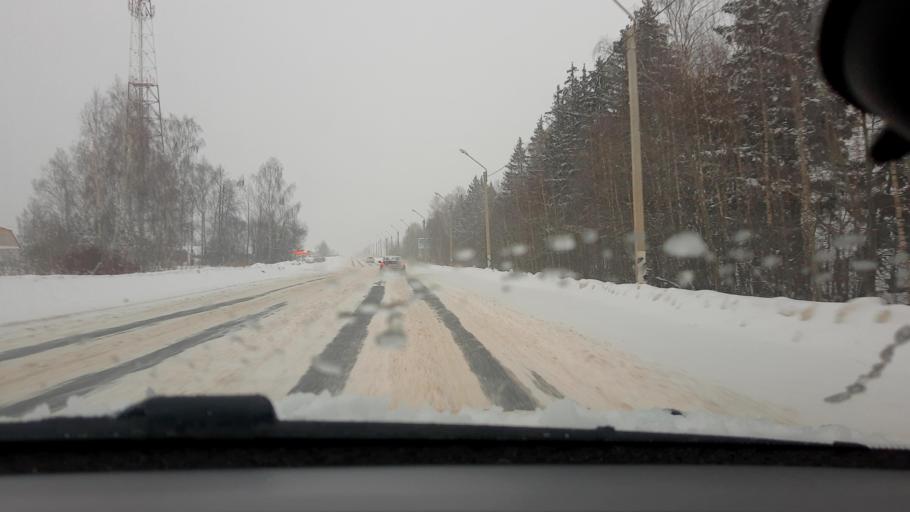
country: RU
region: Nizjnij Novgorod
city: Purekh
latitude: 56.6604
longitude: 43.0975
